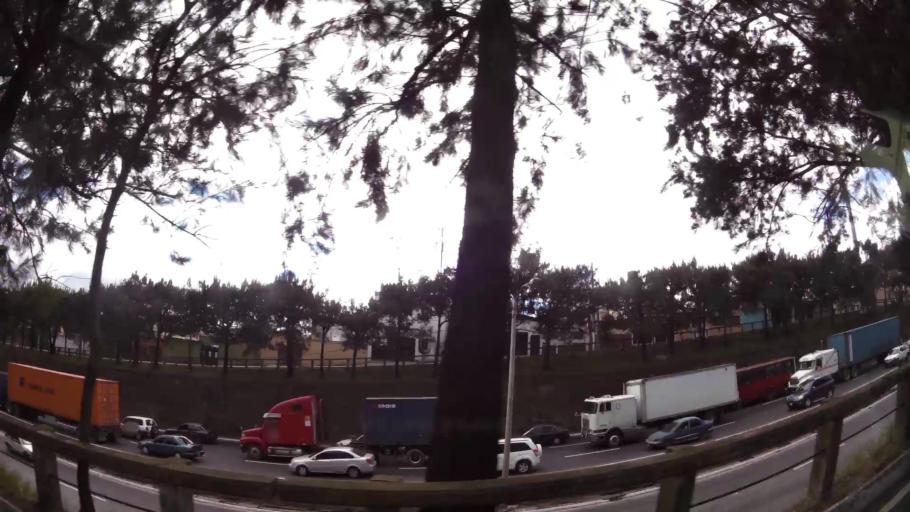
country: GT
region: Guatemala
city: Guatemala City
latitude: 14.6403
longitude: -90.5489
